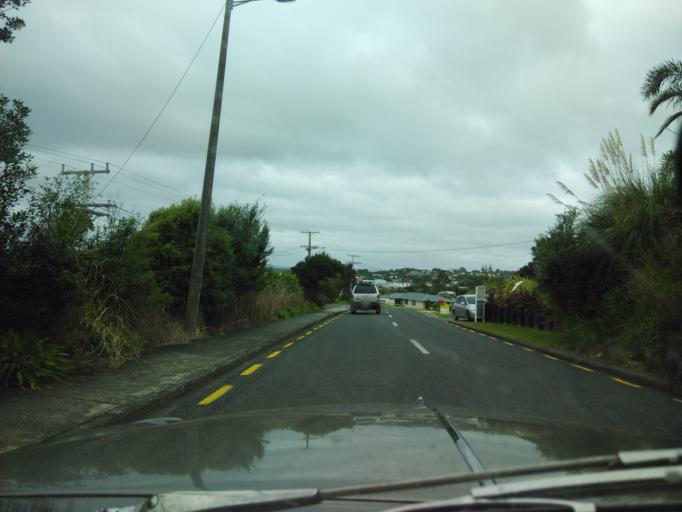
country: NZ
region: Auckland
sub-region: Auckland
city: Wellsford
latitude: -36.0844
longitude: 174.5874
